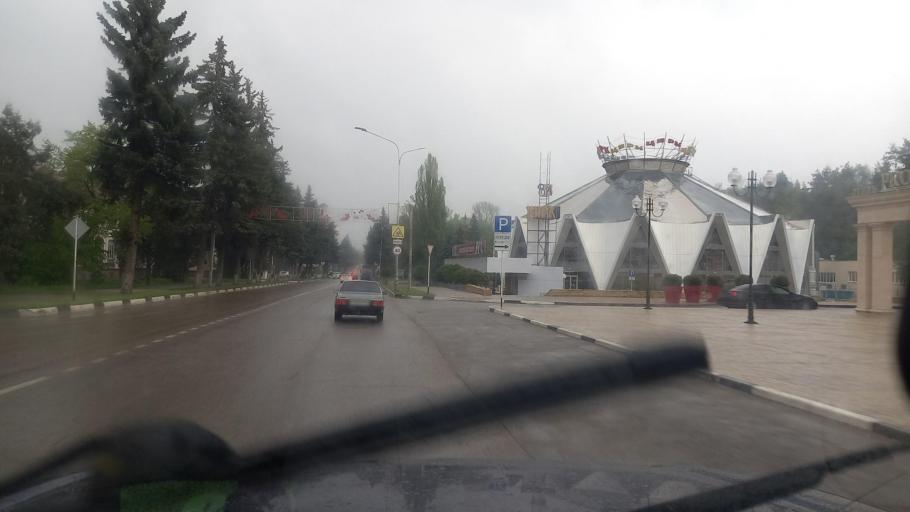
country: RU
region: Stavropol'skiy
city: Kislovodsk
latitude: 43.9131
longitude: 42.7189
